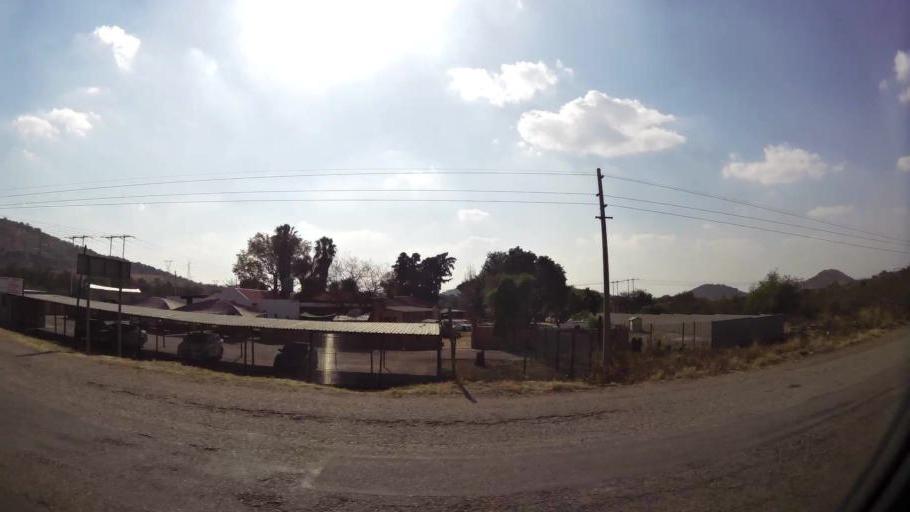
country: ZA
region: North-West
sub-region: Bojanala Platinum District Municipality
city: Rustenburg
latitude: -25.6312
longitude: 27.1847
